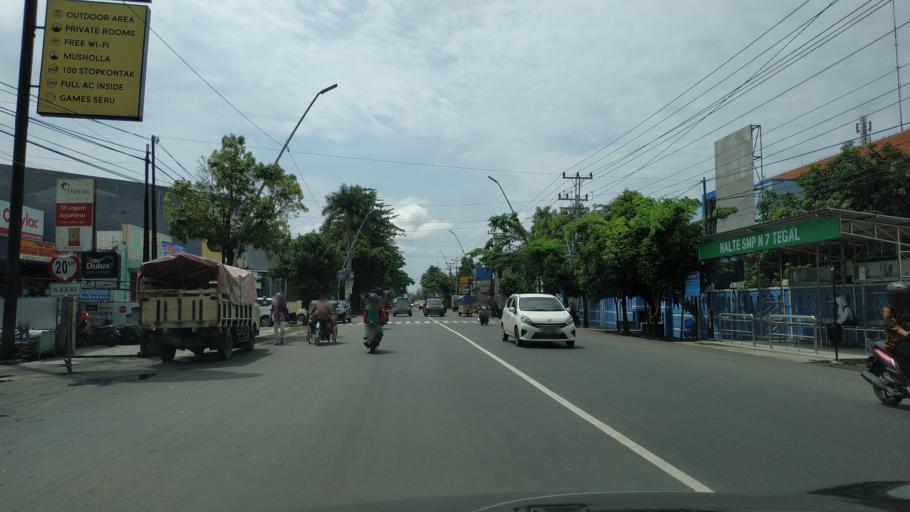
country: ID
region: Central Java
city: Tegal
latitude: -6.8750
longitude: 109.1274
